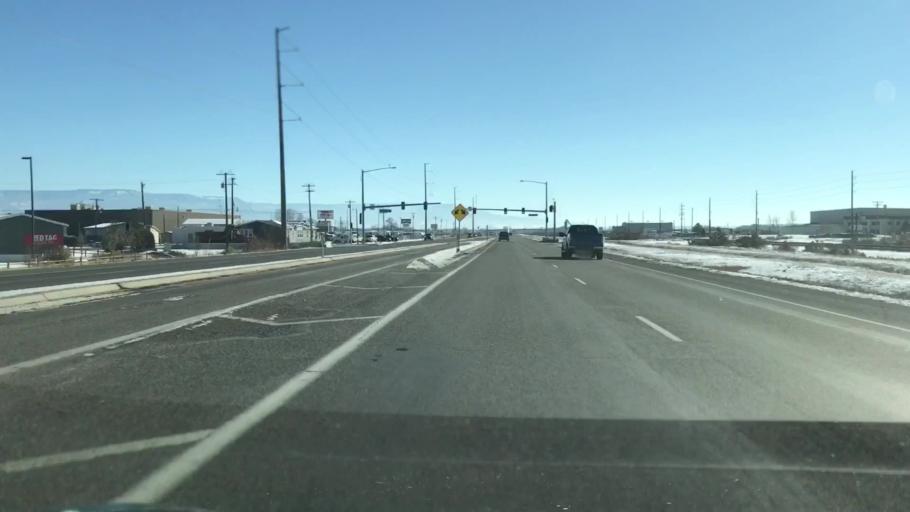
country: US
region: Colorado
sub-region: Mesa County
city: Redlands
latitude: 39.1014
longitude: -108.6281
